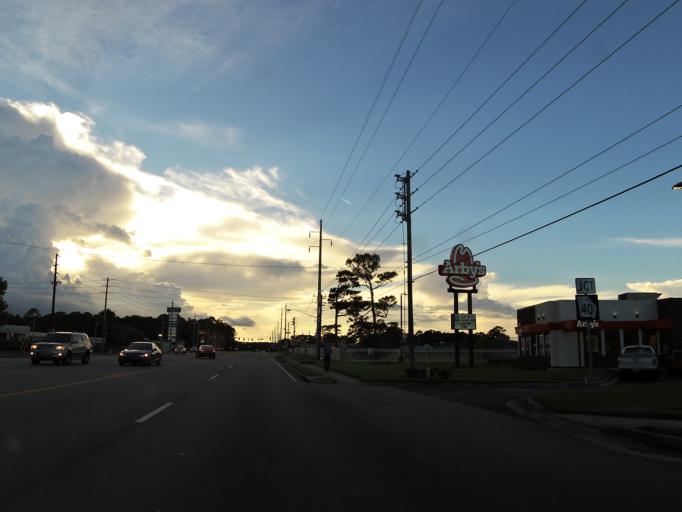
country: US
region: Georgia
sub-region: Camden County
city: St Marys
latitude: 30.7510
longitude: -81.5739
